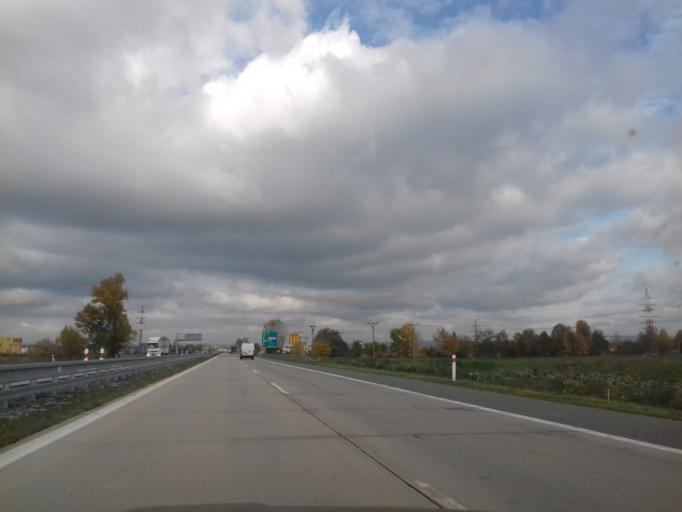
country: CZ
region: South Moravian
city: Rajhradice
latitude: 49.1281
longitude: 16.6417
